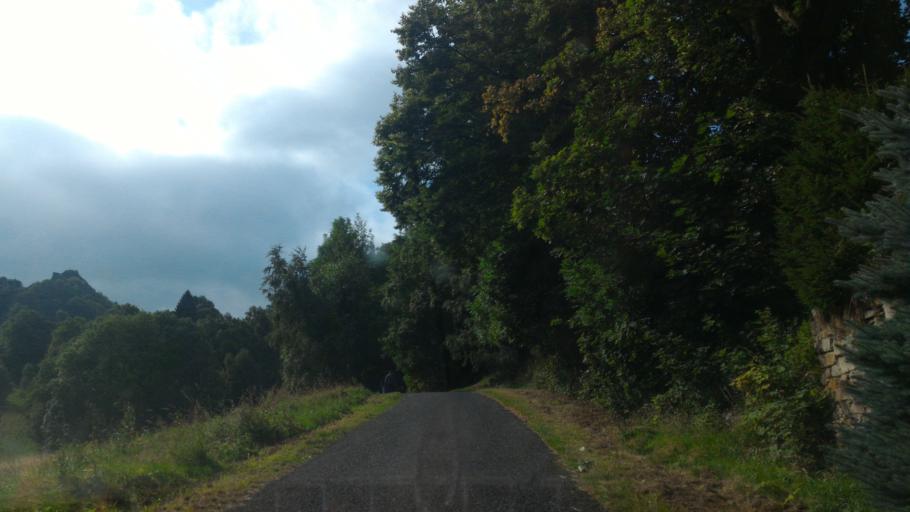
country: CZ
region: Ustecky
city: Dolni Podluzi
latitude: 50.8602
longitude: 14.5766
